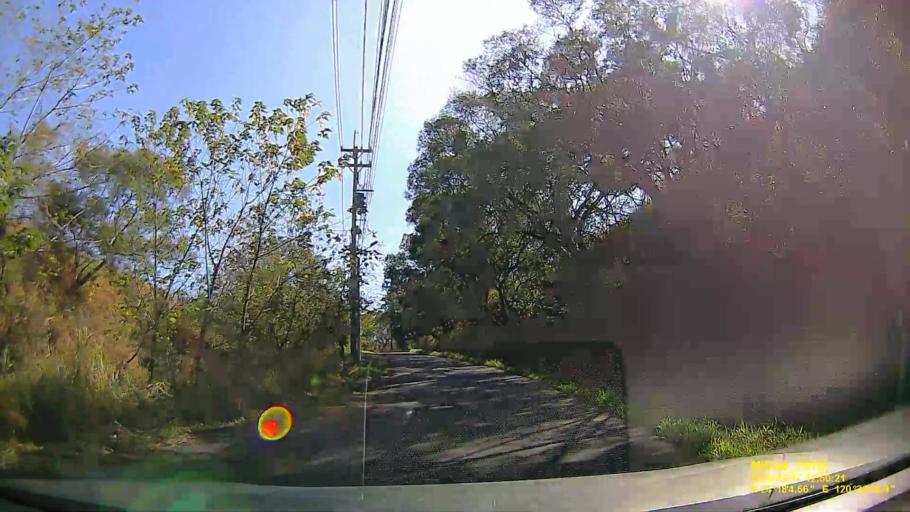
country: TW
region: Taiwan
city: Fengyuan
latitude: 24.3012
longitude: 120.6139
